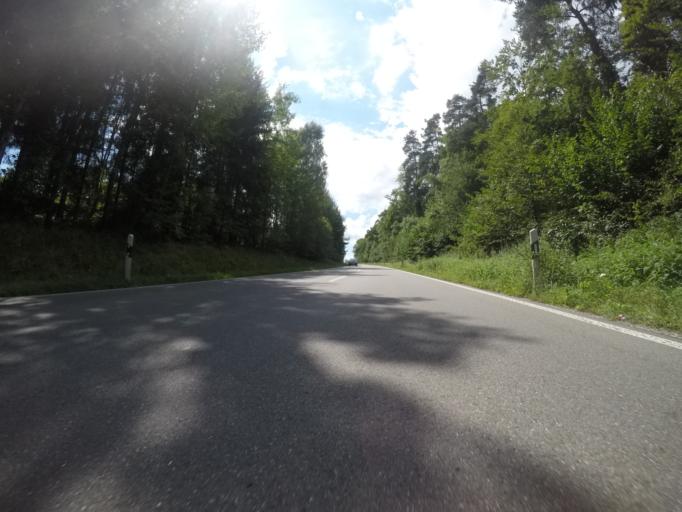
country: DE
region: Baden-Wuerttemberg
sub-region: Karlsruhe Region
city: Neubulach
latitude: 48.6690
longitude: 8.6905
